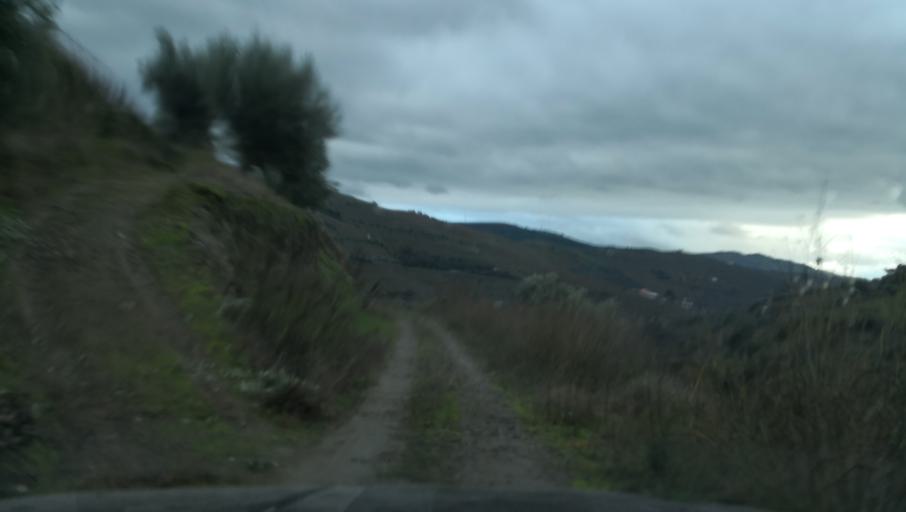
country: PT
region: Vila Real
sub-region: Peso da Regua
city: Peso da Regua
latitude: 41.1941
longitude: -7.7621
